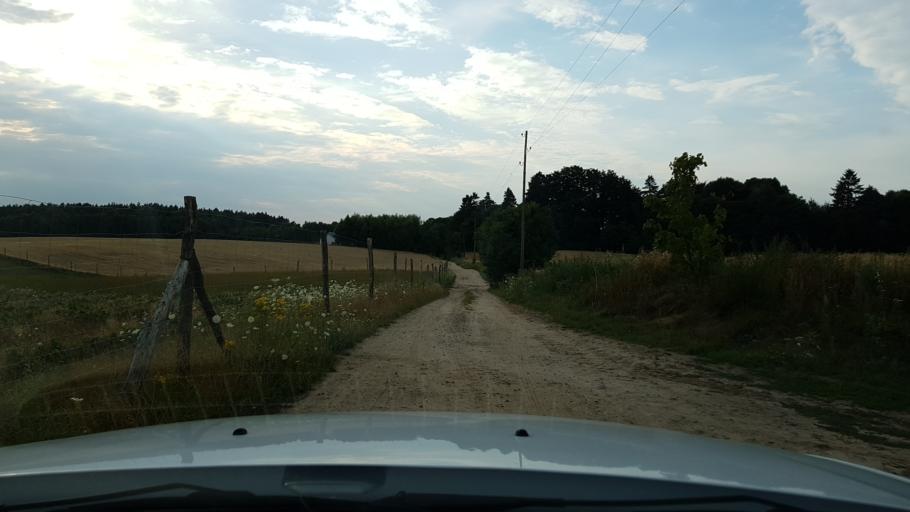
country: PL
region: West Pomeranian Voivodeship
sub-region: Powiat swidwinski
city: Polczyn-Zdroj
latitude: 53.7990
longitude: 16.0788
